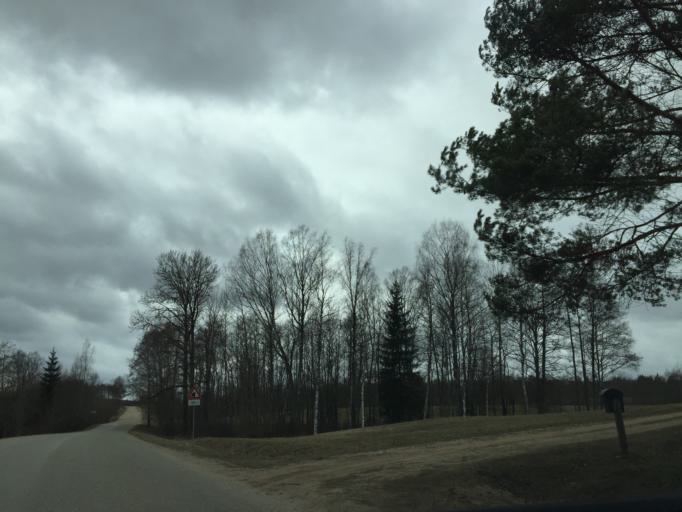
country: LV
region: Kraslavas Rajons
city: Kraslava
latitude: 55.9528
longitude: 27.0111
